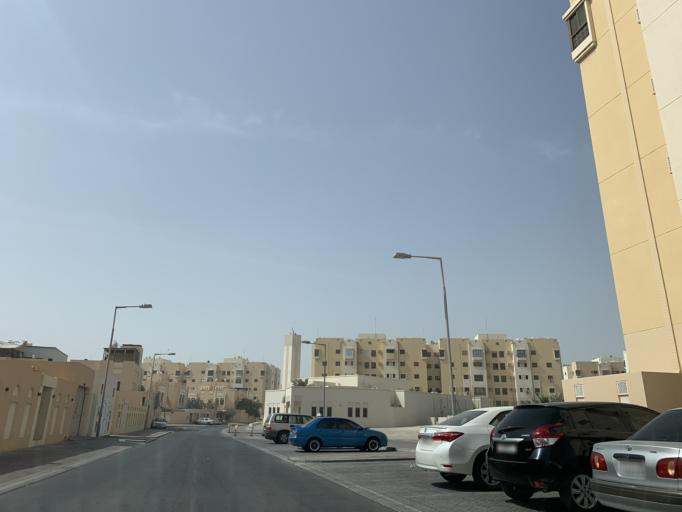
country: BH
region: Northern
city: Madinat `Isa
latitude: 26.1739
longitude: 50.5218
